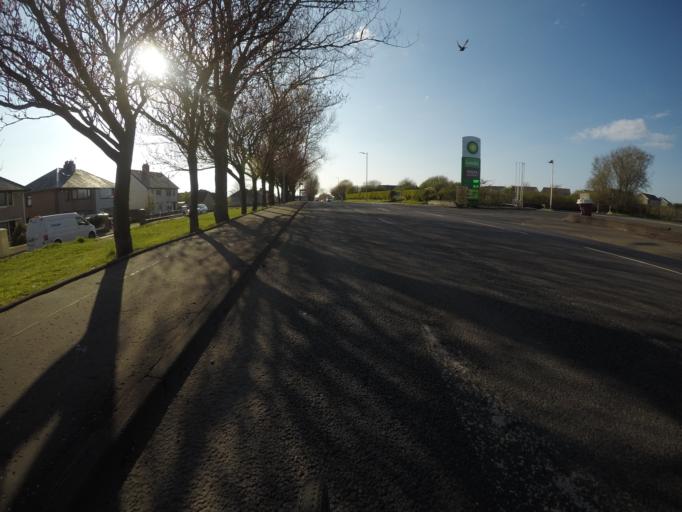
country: GB
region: Scotland
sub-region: North Ayrshire
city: Saltcoats
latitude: 55.6412
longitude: -4.7762
